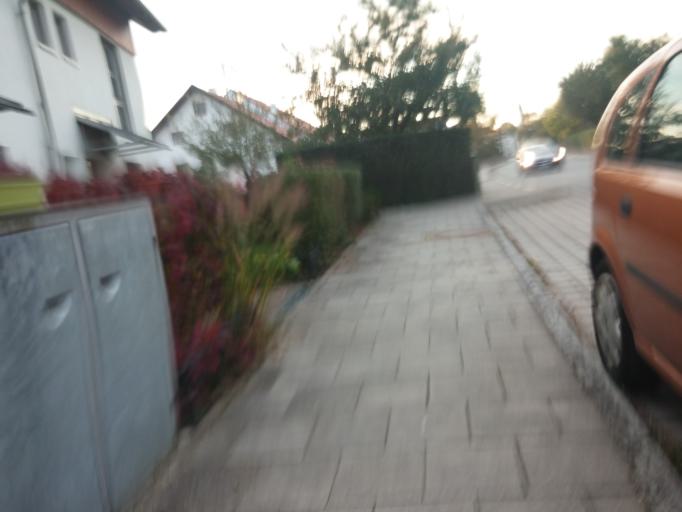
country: DE
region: Bavaria
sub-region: Upper Bavaria
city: Grasbrunn
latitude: 48.0784
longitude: 11.7470
